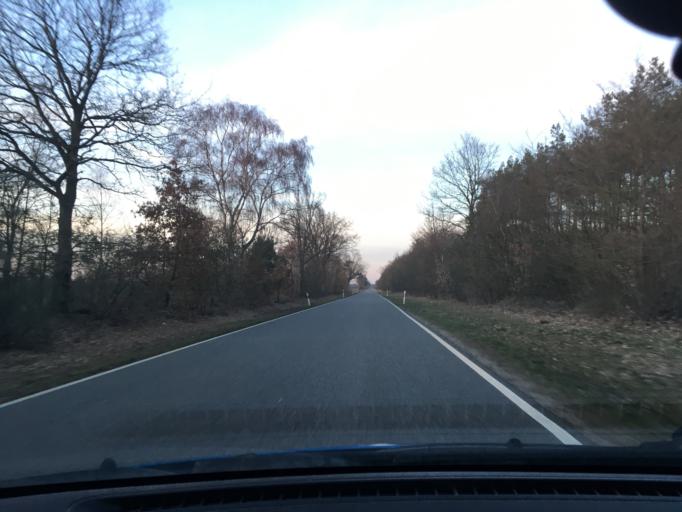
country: DE
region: Schleswig-Holstein
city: Langenlehsten
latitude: 53.5115
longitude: 10.7436
